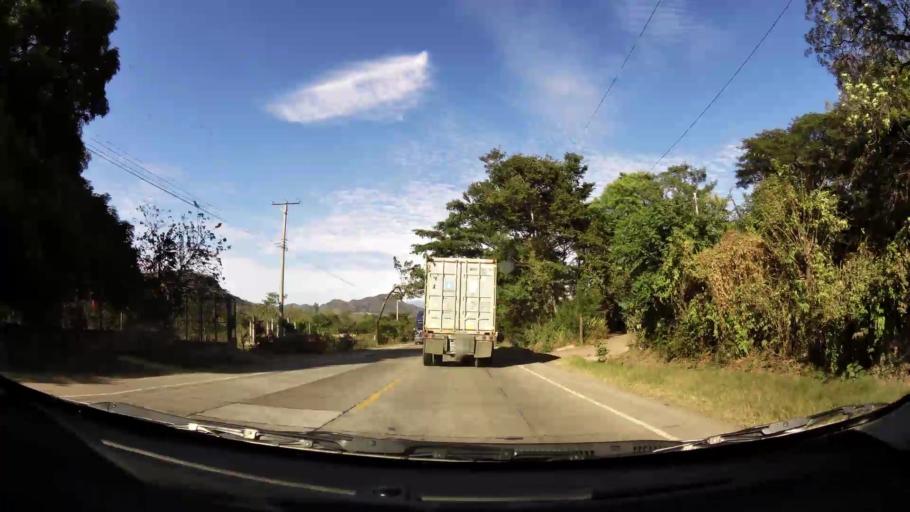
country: SV
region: Santa Ana
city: Texistepeque
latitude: 14.0770
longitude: -89.5017
